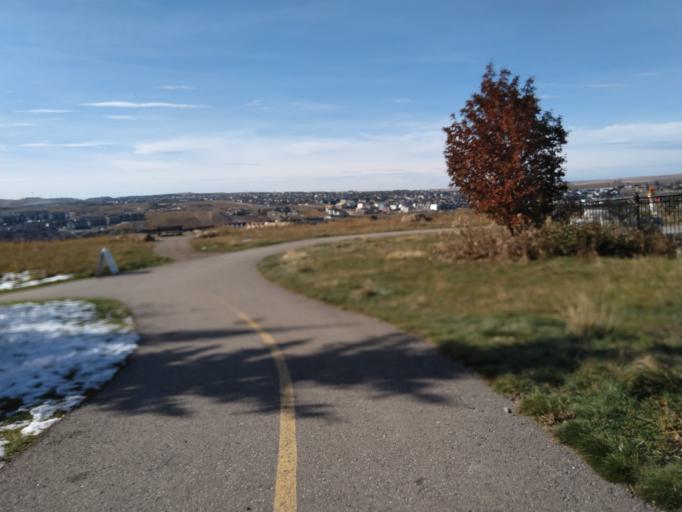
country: CA
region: Alberta
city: Calgary
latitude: 51.1736
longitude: -114.1233
